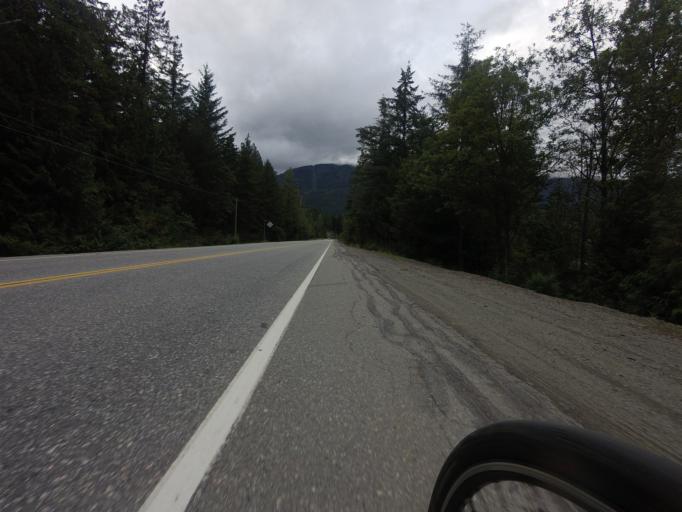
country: CA
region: British Columbia
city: Pemberton
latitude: 50.2564
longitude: -122.8617
